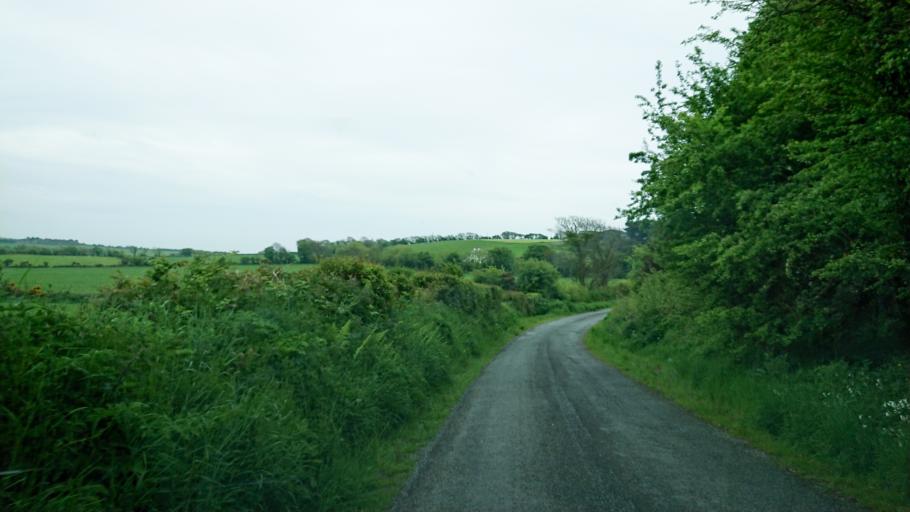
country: IE
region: Munster
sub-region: Waterford
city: Dunmore East
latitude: 52.2225
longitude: -7.0149
